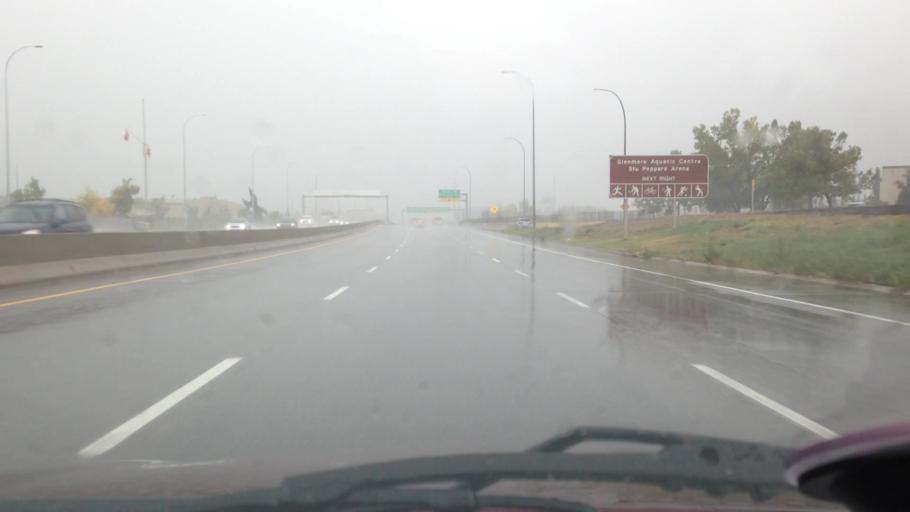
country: CA
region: Alberta
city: Calgary
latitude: 51.0151
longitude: -114.1182
